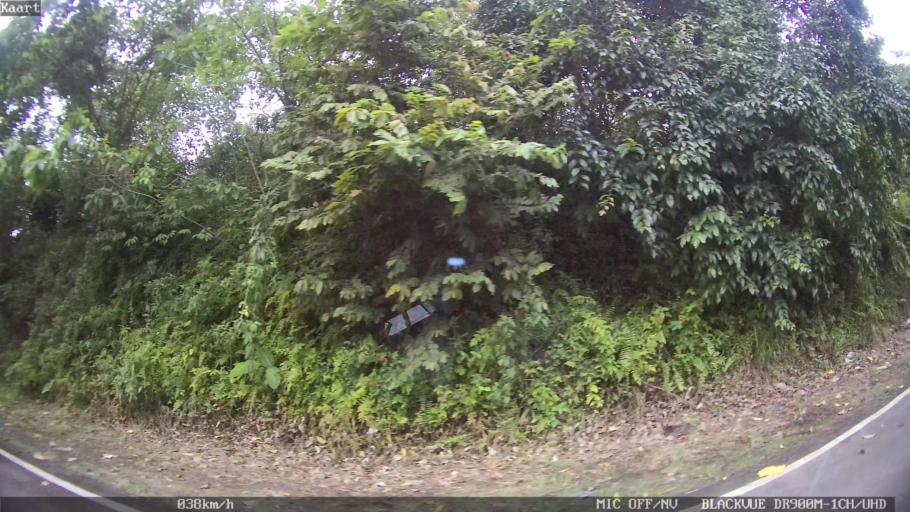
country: ID
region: Lampung
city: Bandarlampung
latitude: -5.4285
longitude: 105.2009
